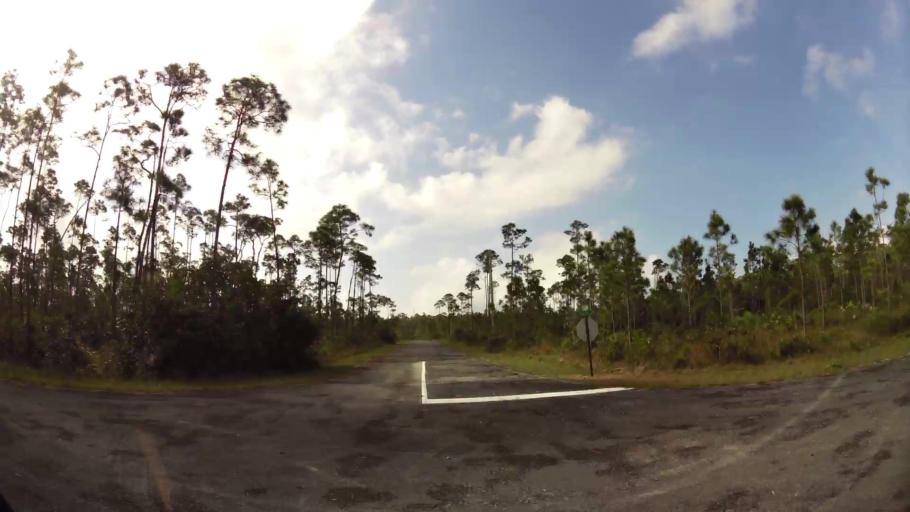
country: BS
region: Freeport
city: Lucaya
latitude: 26.5847
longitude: -78.5522
